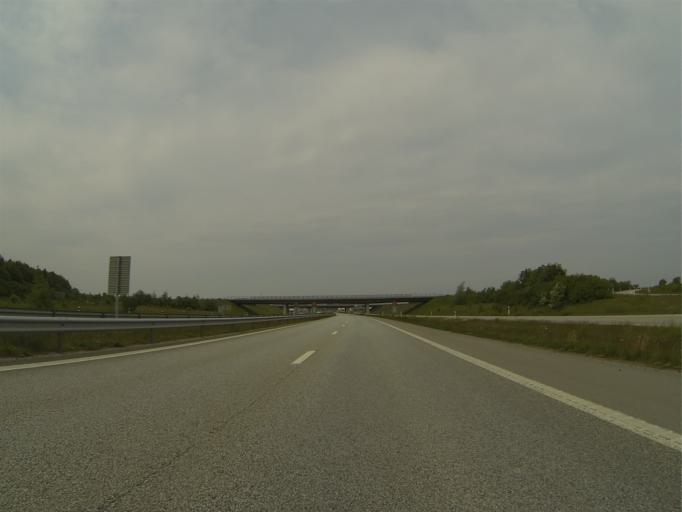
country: SE
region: Skane
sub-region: Burlovs Kommun
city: Arloev
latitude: 55.6152
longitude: 13.1191
